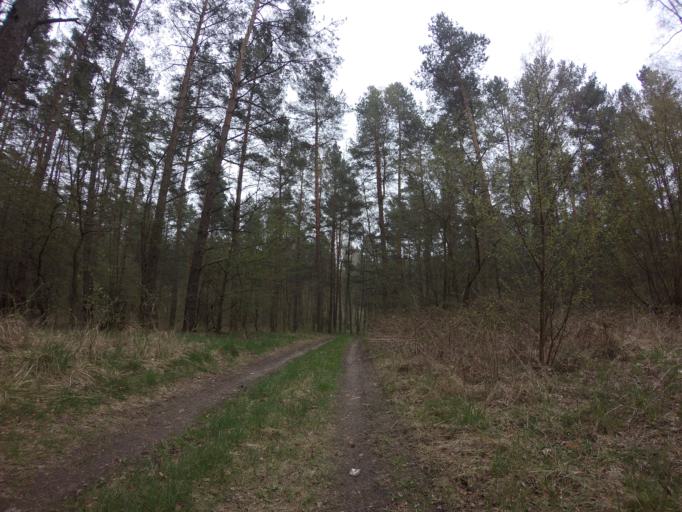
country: PL
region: West Pomeranian Voivodeship
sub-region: Powiat choszczenski
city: Recz
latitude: 53.1863
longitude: 15.5295
